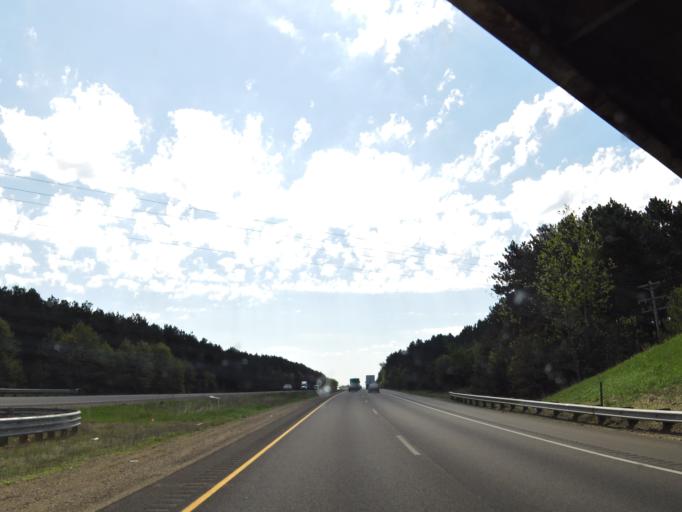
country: US
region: Wisconsin
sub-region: Eau Claire County
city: Altoona
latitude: 44.7631
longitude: -91.4042
